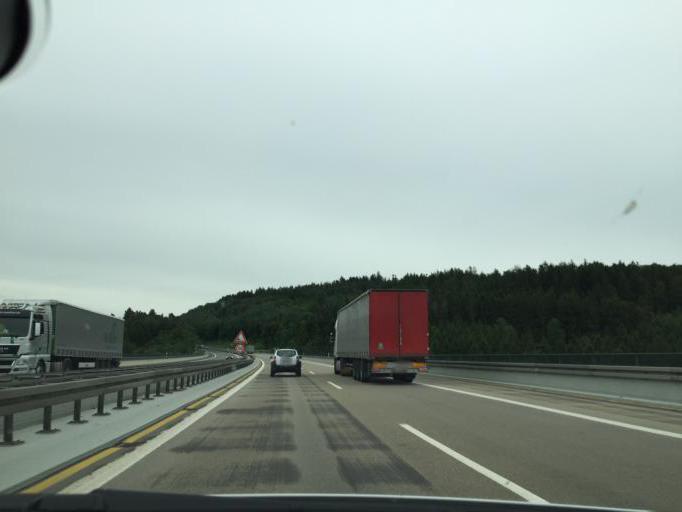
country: DE
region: Bavaria
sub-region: Regierungsbezirk Unterfranken
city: Motten
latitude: 50.3520
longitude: 9.7412
